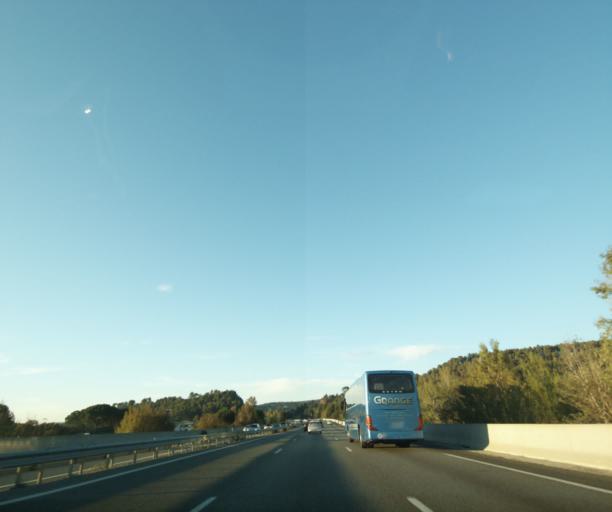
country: FR
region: Provence-Alpes-Cote d'Azur
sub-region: Departement des Bouches-du-Rhone
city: Meyreuil
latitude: 43.4935
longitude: 5.5262
